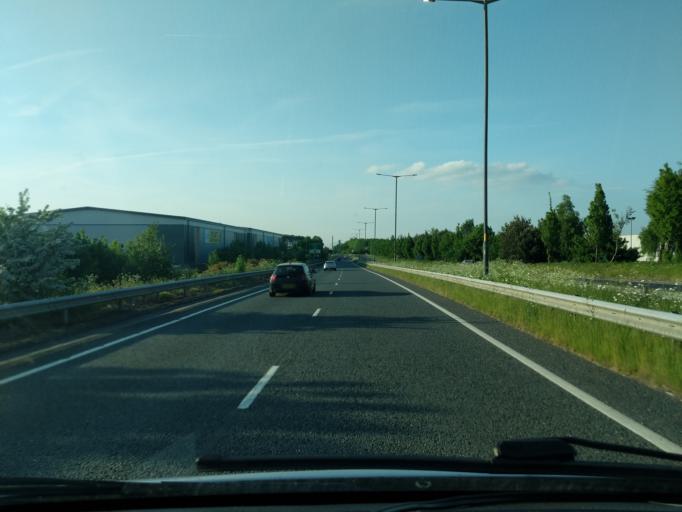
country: GB
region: England
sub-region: St. Helens
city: St Helens
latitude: 53.4245
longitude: -2.7406
